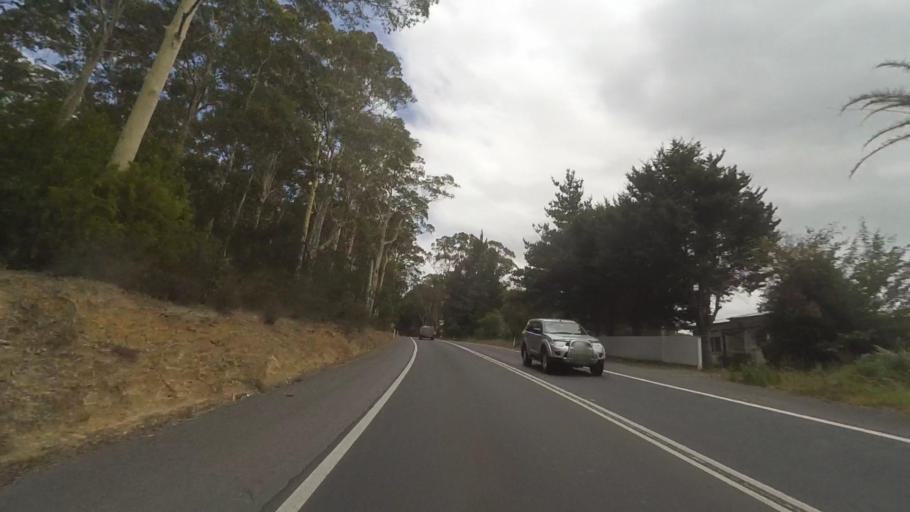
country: AU
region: New South Wales
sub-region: Shoalhaven Shire
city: Falls Creek
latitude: -35.0817
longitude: 150.5181
